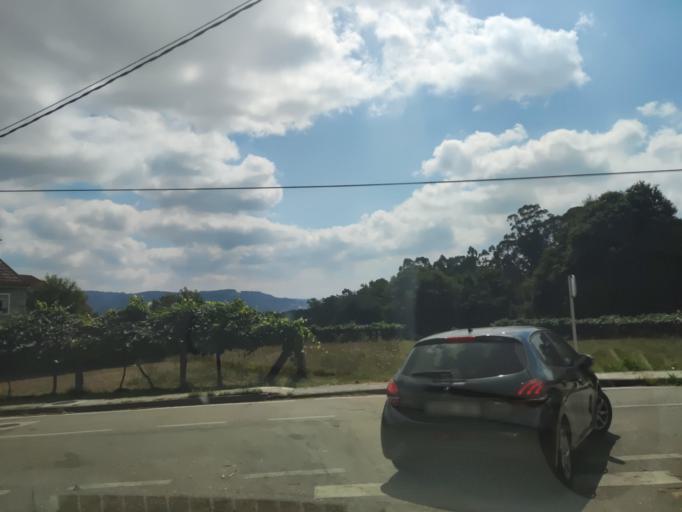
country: ES
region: Galicia
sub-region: Provincia de Pontevedra
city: Porrino
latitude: 42.1508
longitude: -8.6496
